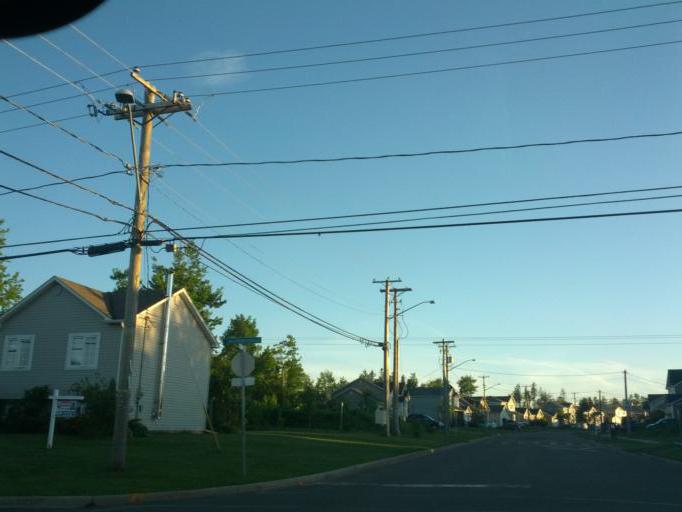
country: CA
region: New Brunswick
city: Moncton
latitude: 46.1174
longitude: -64.8711
